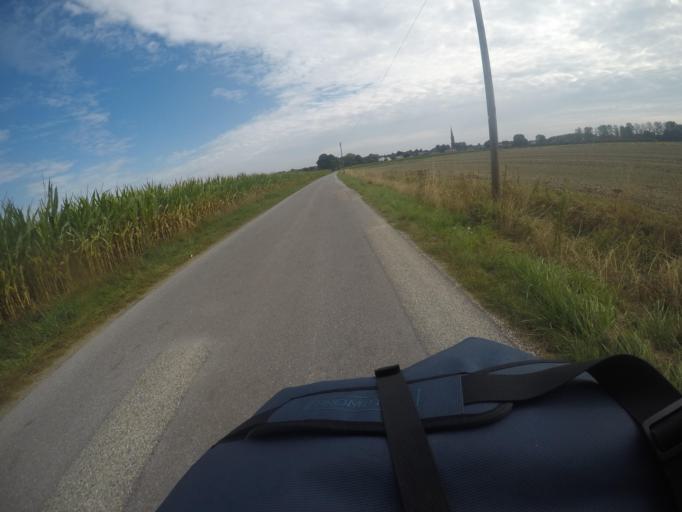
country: DE
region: North Rhine-Westphalia
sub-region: Regierungsbezirk Dusseldorf
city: Emmerich
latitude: 51.8465
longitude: 6.1935
